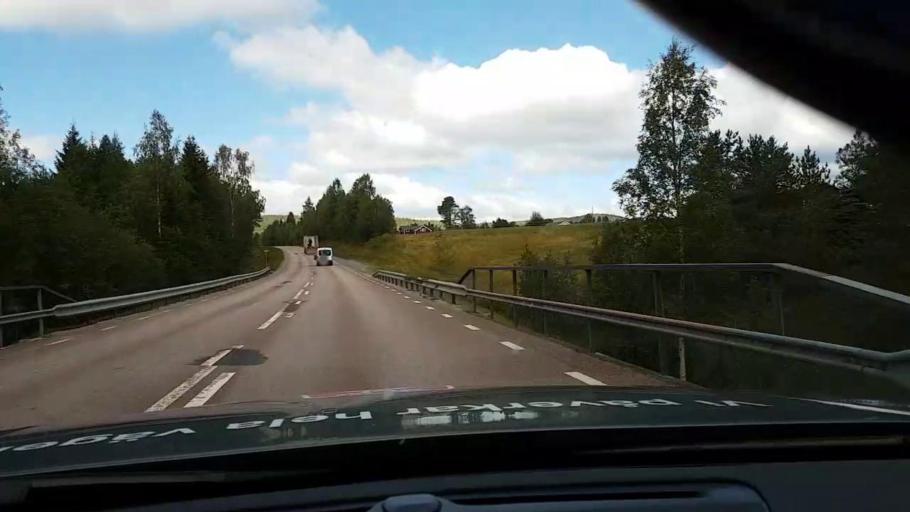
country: SE
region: Vaesternorrland
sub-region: OErnskoeldsviks Kommun
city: Bjasta
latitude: 63.3725
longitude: 18.4357
